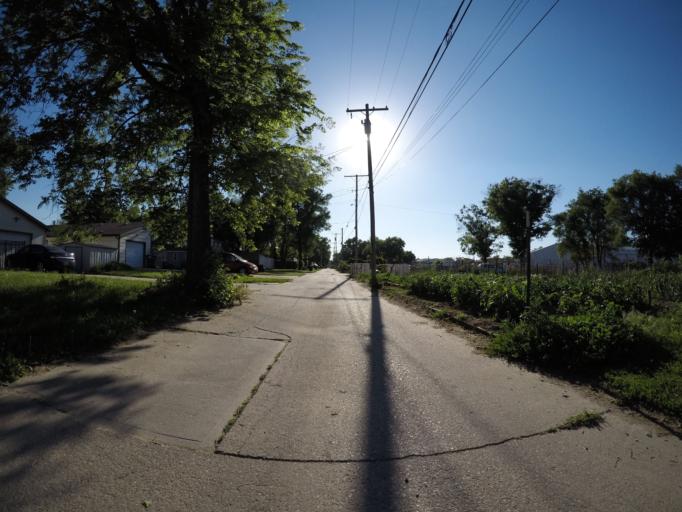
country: US
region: Kansas
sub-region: Riley County
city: Manhattan
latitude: 39.1727
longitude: -96.5681
